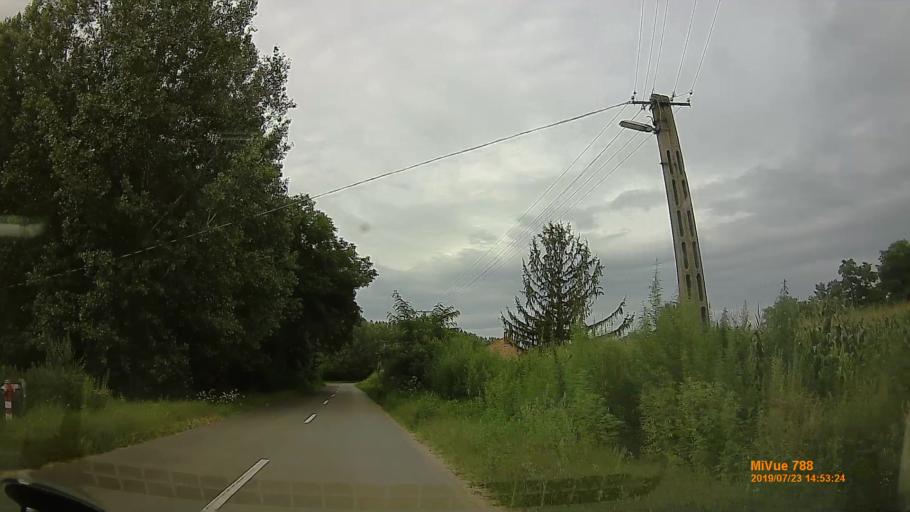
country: HU
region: Szabolcs-Szatmar-Bereg
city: Kalmanhaza
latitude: 47.8784
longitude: 21.6528
